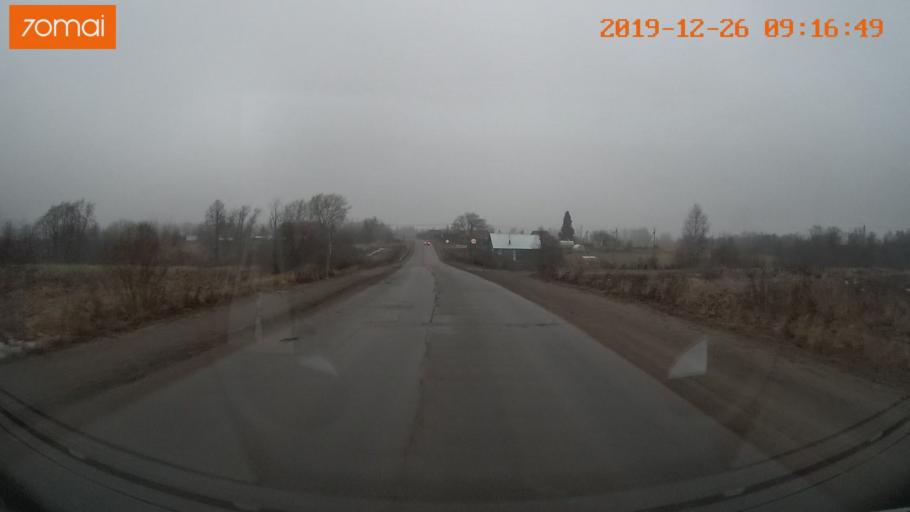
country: RU
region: Vologda
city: Gryazovets
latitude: 58.9229
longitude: 40.2393
